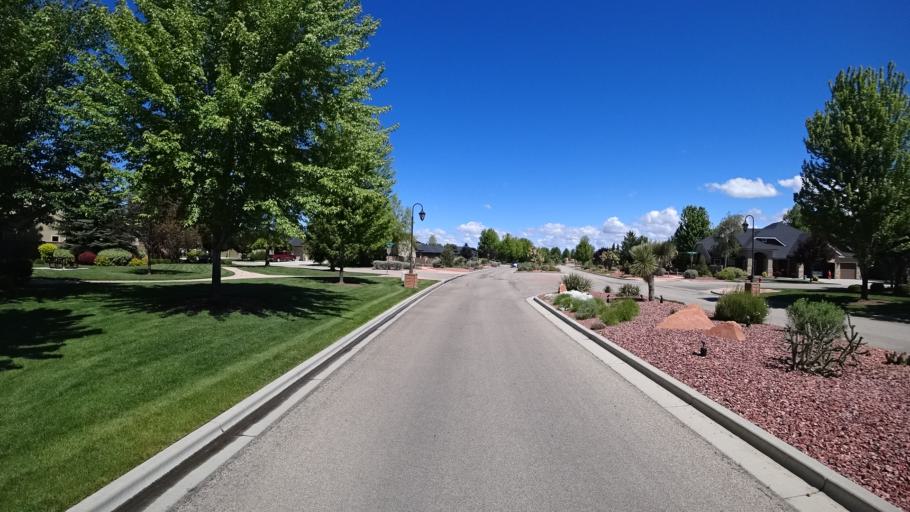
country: US
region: Idaho
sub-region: Ada County
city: Meridian
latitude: 43.6510
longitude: -116.3845
